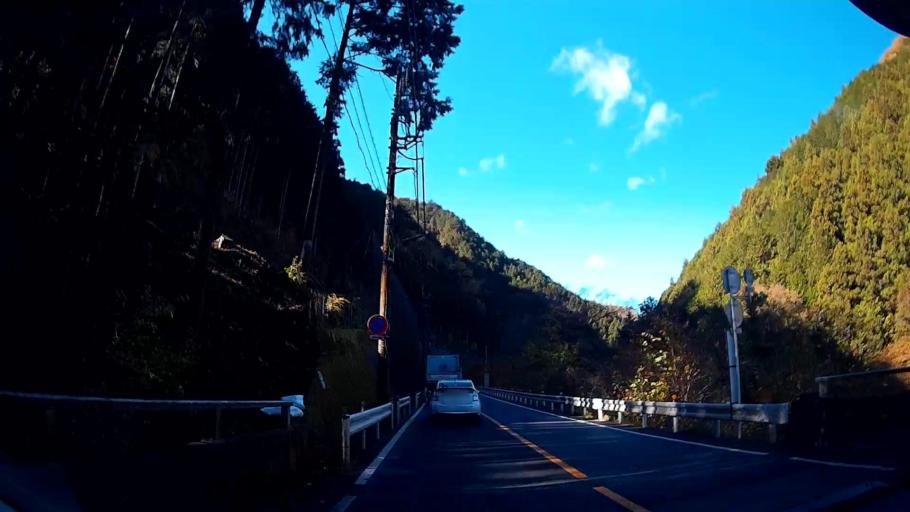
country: JP
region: Tokyo
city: Itsukaichi
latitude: 35.7224
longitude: 139.1670
